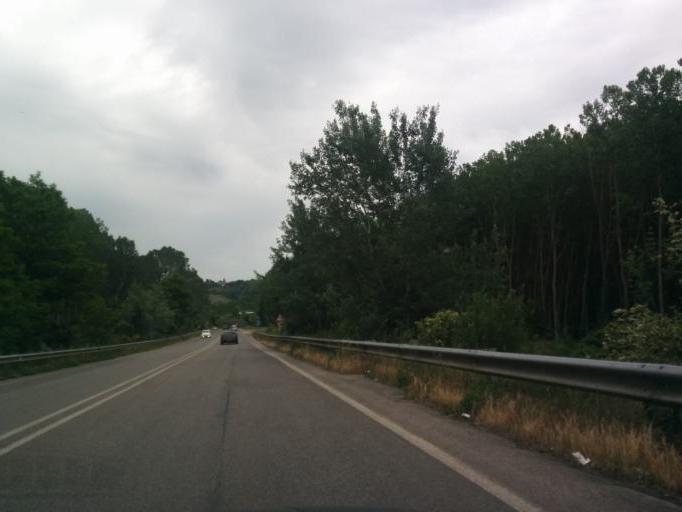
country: IT
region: Tuscany
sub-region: Provincia di Siena
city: Poggibonsi
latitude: 43.4594
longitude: 11.1031
